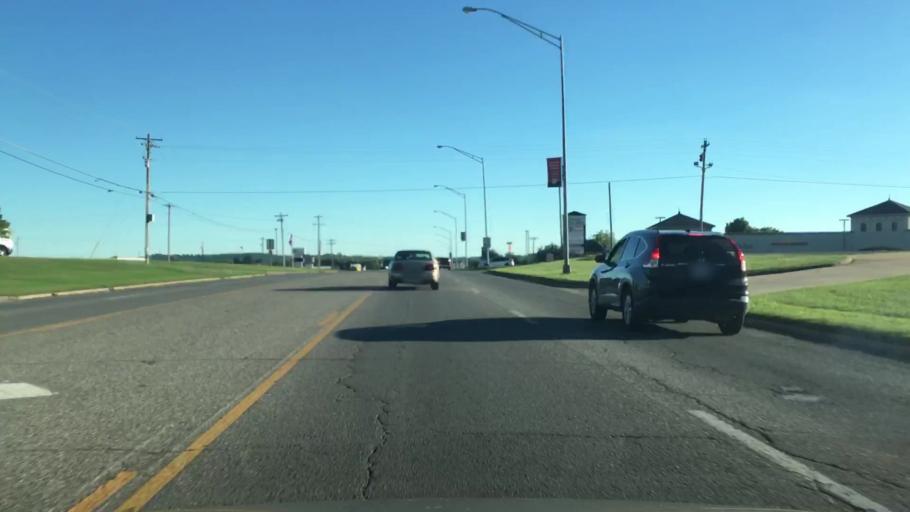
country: US
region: Oklahoma
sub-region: Cherokee County
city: Park Hill
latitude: 35.8825
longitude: -94.9764
